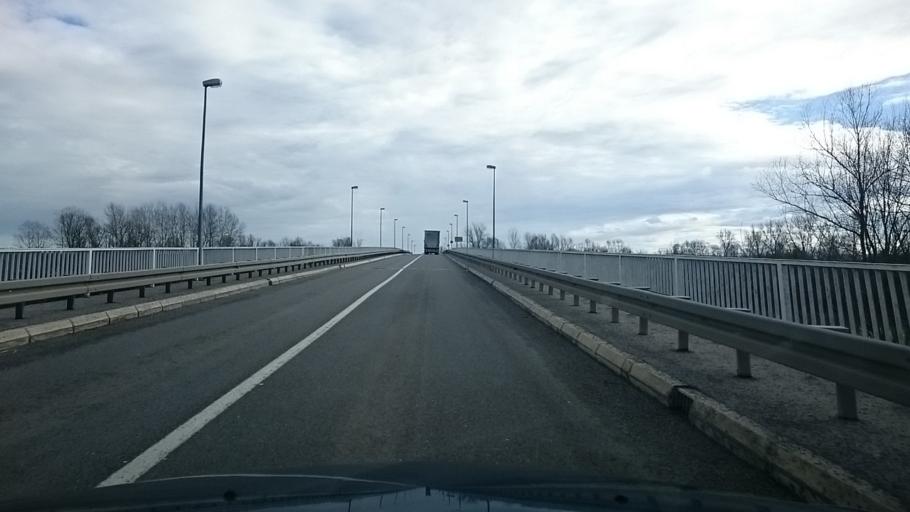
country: HR
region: Sisacko-Moslavacka
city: Novska
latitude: 45.2696
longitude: 16.9139
